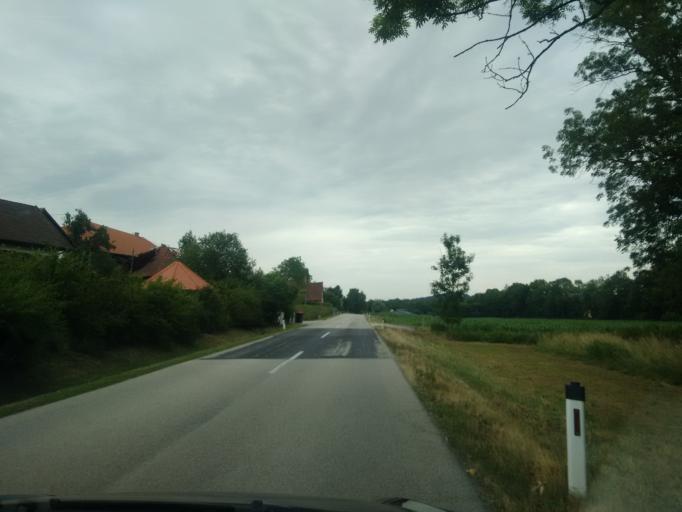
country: AT
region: Upper Austria
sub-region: Politischer Bezirk Grieskirchen
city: Bad Schallerbach
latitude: 48.1964
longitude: 13.8910
